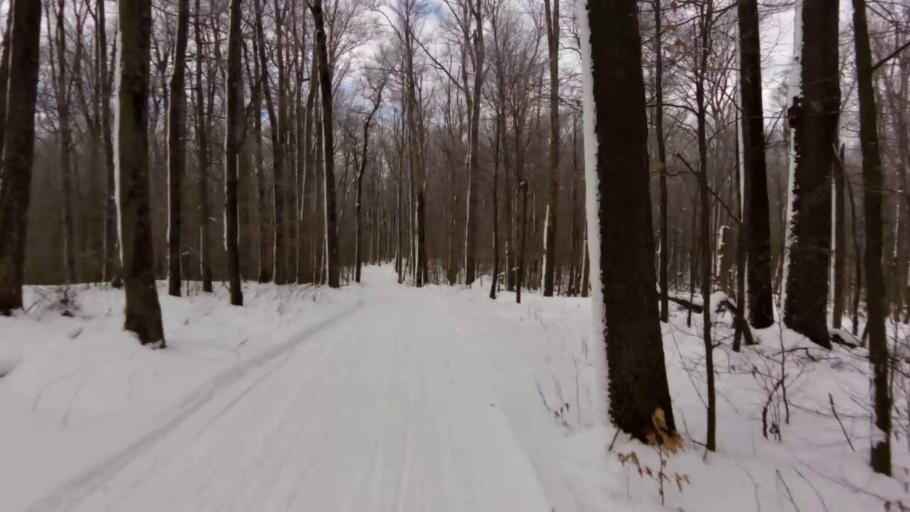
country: US
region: New York
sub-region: Cattaraugus County
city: Salamanca
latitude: 42.0357
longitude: -78.7527
